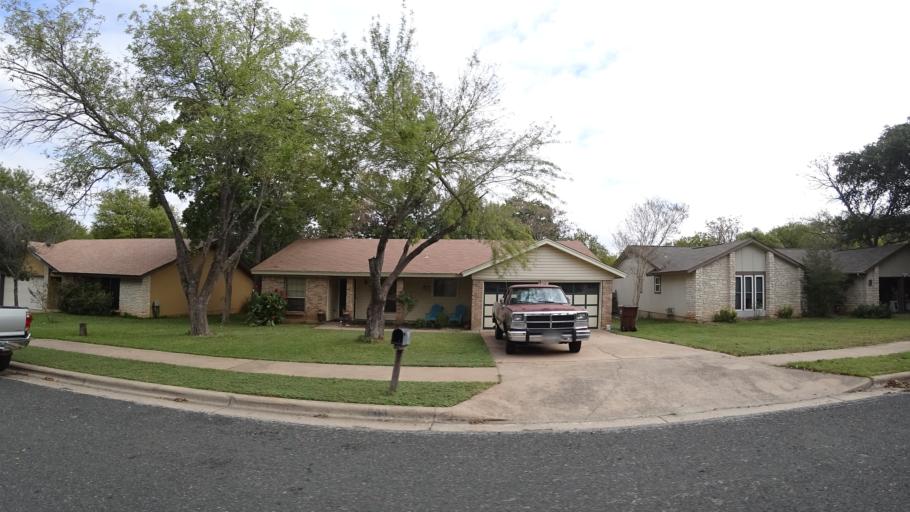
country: US
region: Texas
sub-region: Williamson County
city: Brushy Creek
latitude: 30.5170
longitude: -97.7365
